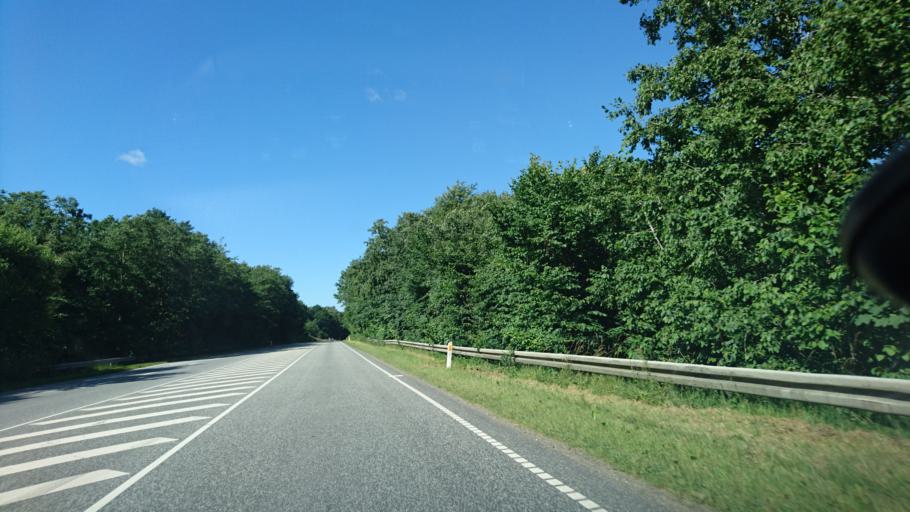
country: DK
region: North Denmark
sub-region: Alborg Kommune
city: Gistrup
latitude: 56.9828
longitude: 10.0062
